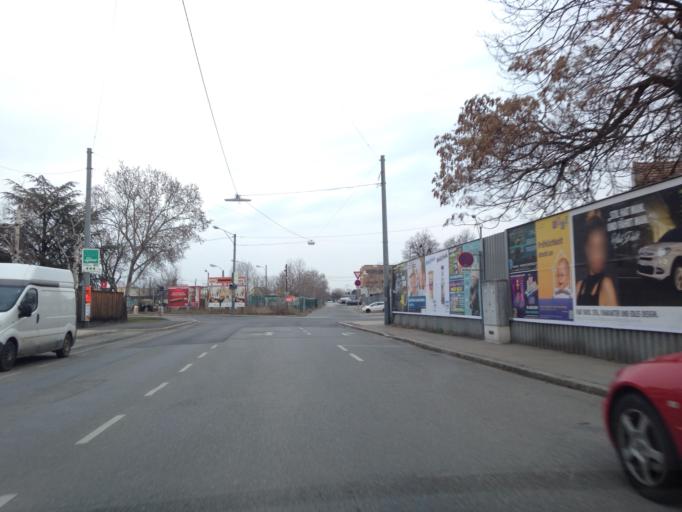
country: AT
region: Lower Austria
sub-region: Politischer Bezirk Wien-Umgebung
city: Gerasdorf bei Wien
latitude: 48.2498
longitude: 16.4527
